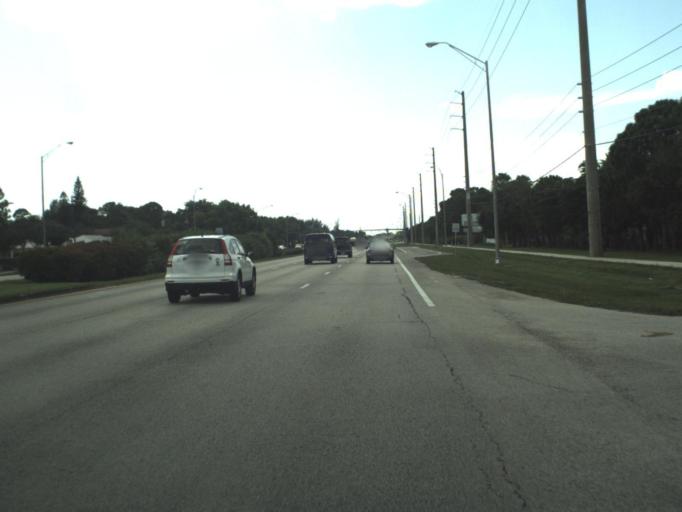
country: US
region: Florida
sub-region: Martin County
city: Port Salerno
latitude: 27.1273
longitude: -80.1963
